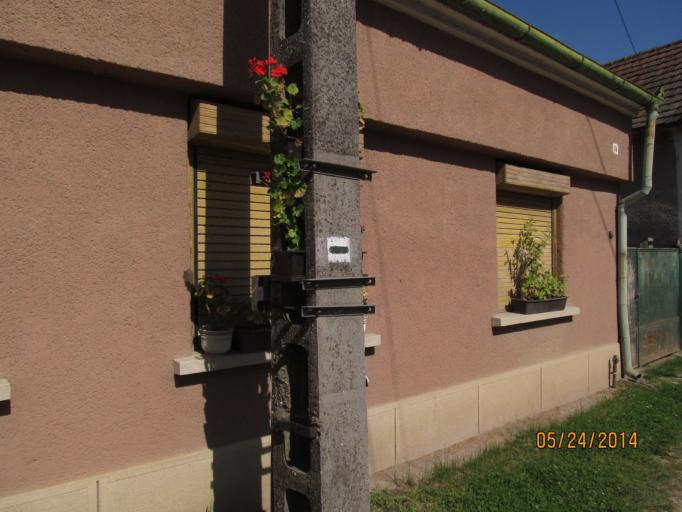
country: HU
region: Vas
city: Vasvar
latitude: 47.0464
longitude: 16.8004
